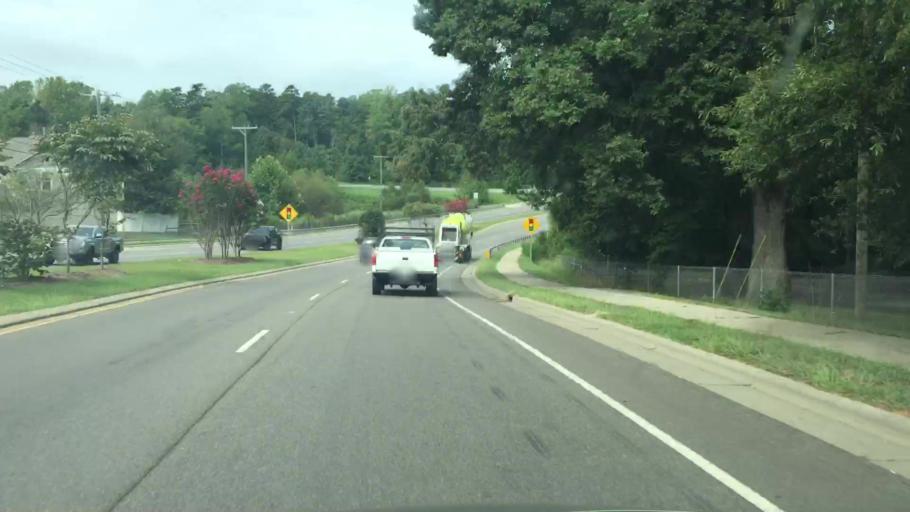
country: US
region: North Carolina
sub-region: Iredell County
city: Mooresville
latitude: 35.5814
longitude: -80.8592
